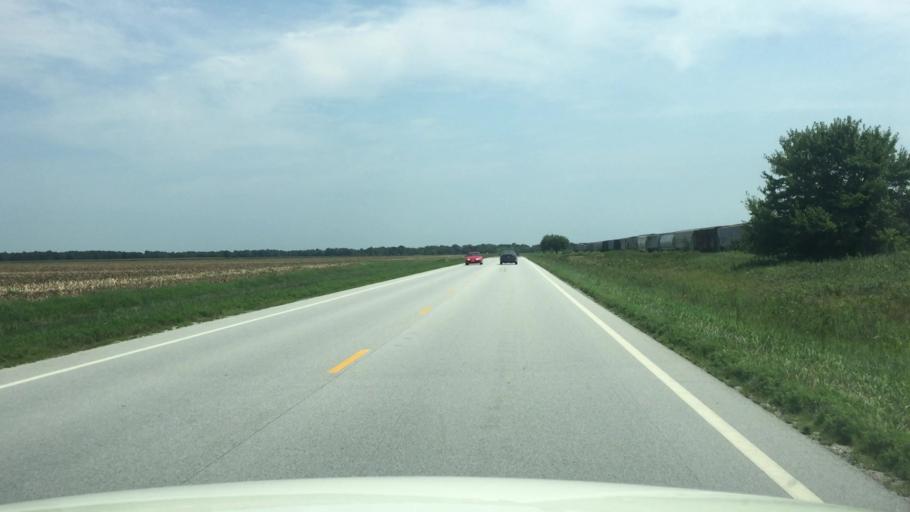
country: US
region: Kansas
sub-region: Labette County
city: Oswego
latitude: 37.1683
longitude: -95.0258
